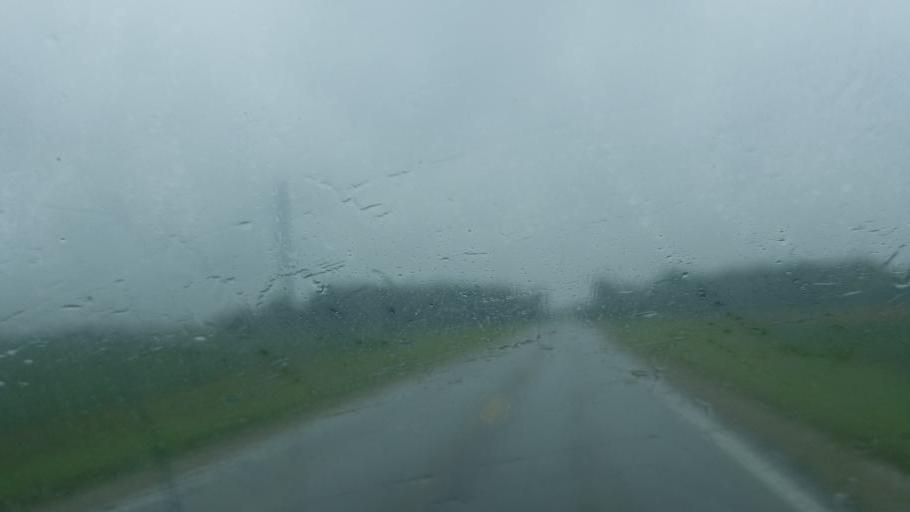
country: US
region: Indiana
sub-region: Huntington County
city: Warren
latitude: 40.6542
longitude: -85.3848
